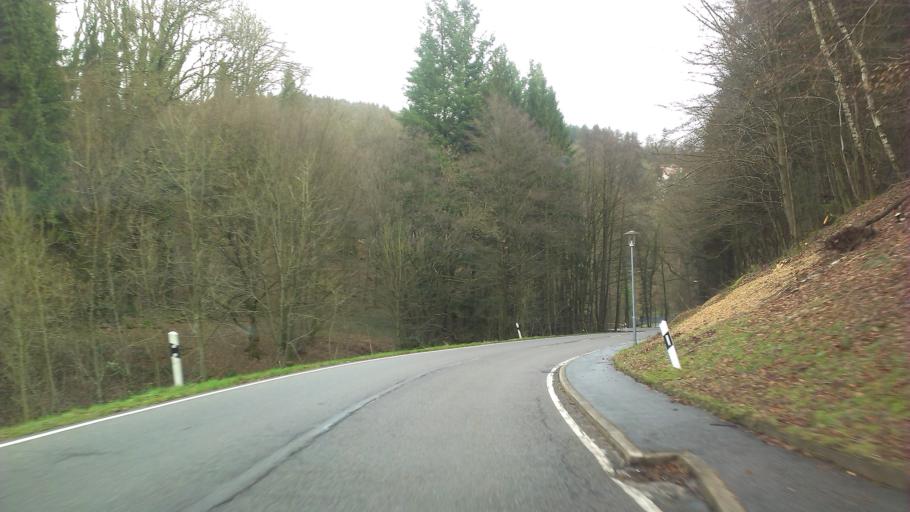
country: DE
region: Baden-Wuerttemberg
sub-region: Karlsruhe Region
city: Heiligkreuzsteinach
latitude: 49.4876
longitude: 8.7885
